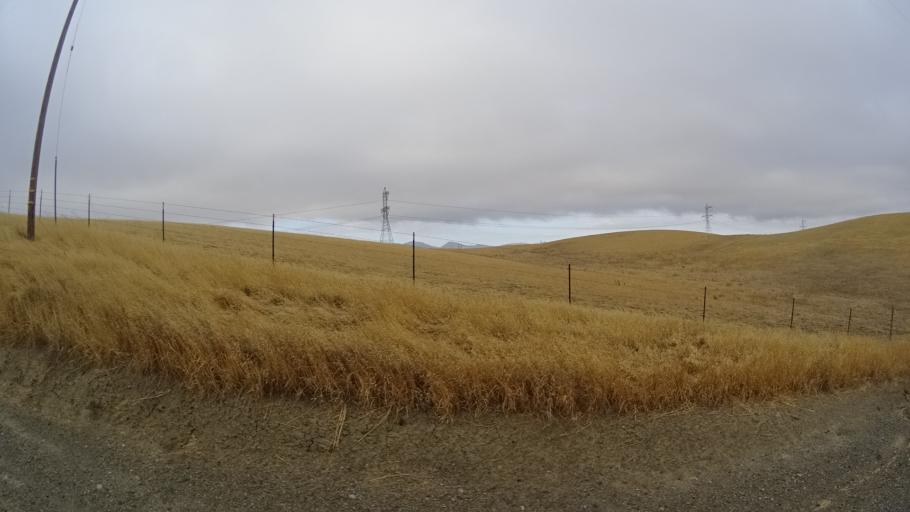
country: US
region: California
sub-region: Yolo County
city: Dunnigan
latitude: 38.8554
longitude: -122.0457
